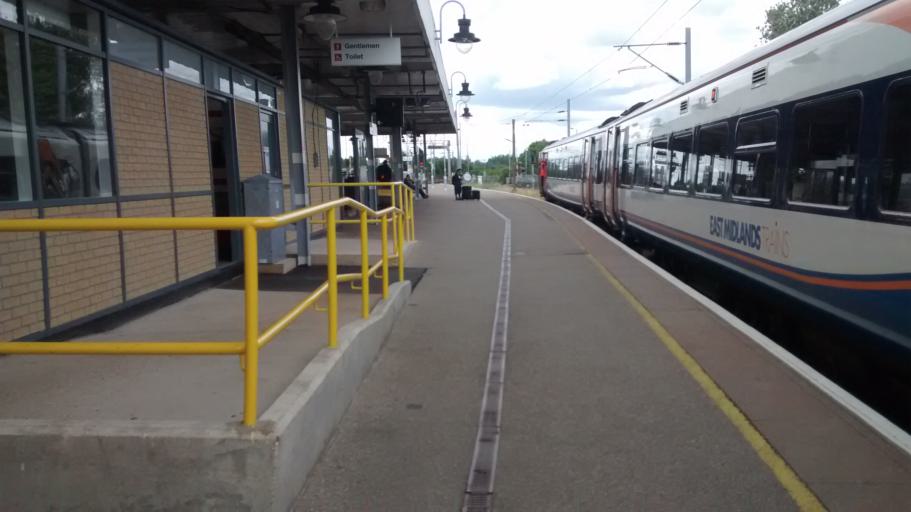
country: GB
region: England
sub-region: Cambridgeshire
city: Ely
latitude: 52.3903
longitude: 0.2663
